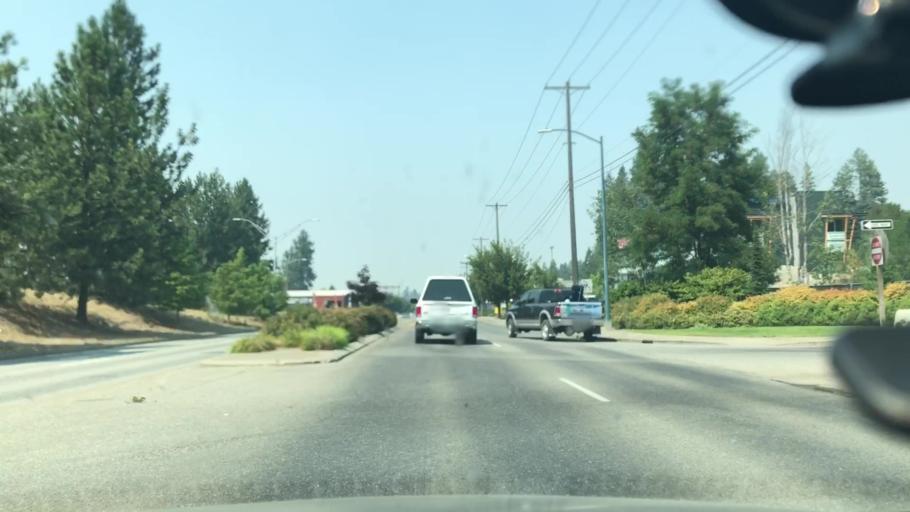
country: US
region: Idaho
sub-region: Kootenai County
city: Coeur d'Alene
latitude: 47.6874
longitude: -116.7970
